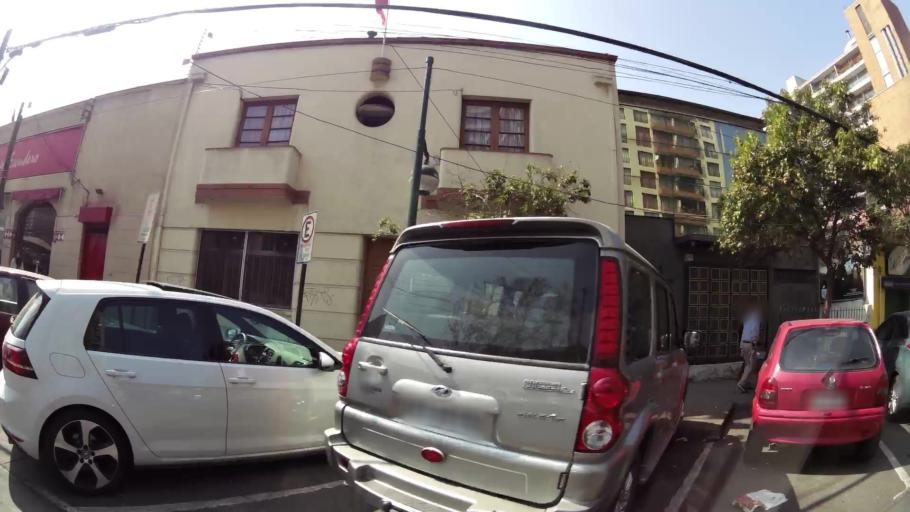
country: CL
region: Santiago Metropolitan
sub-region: Provincia de Santiago
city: Villa Presidente Frei, Nunoa, Santiago, Chile
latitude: -33.4551
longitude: -70.5996
